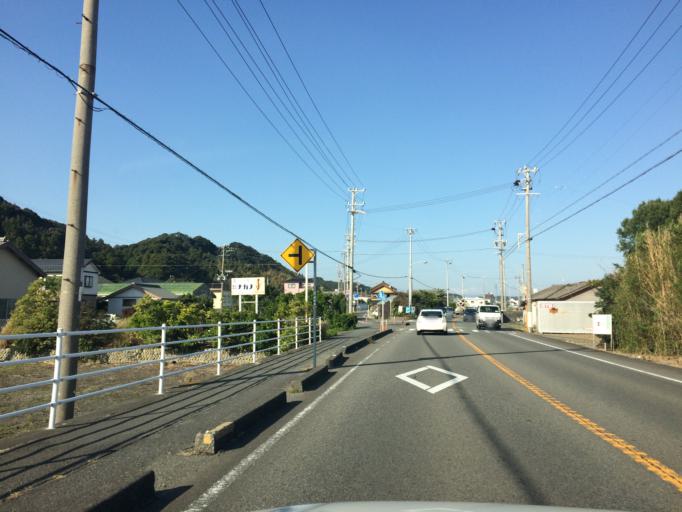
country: JP
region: Shizuoka
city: Sagara
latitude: 34.7090
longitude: 138.2133
